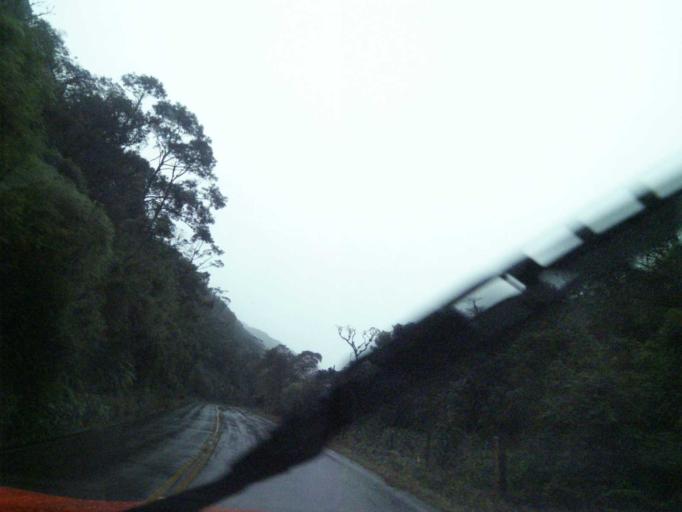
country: BR
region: Santa Catarina
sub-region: Anitapolis
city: Anitapolis
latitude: -27.7670
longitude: -49.0397
